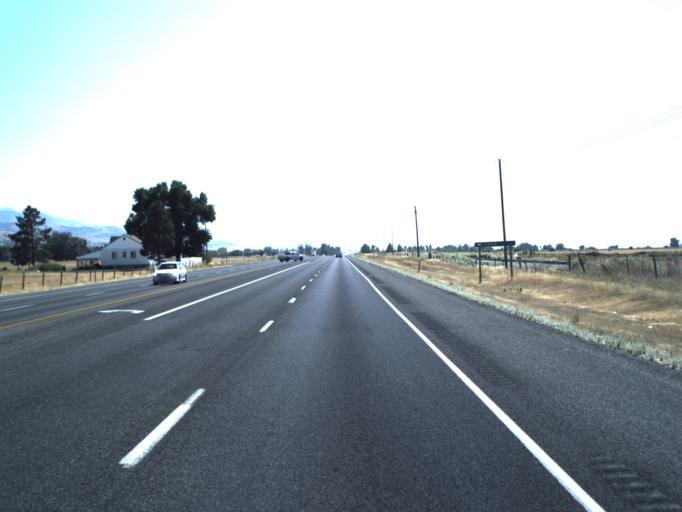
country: US
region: Utah
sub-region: Cache County
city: Lewiston
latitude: 41.9705
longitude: -111.8129
